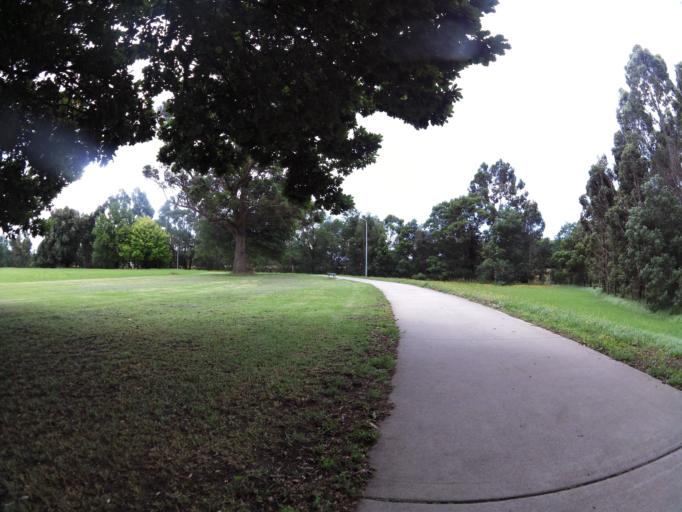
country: AU
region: Victoria
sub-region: Latrobe
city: Traralgon
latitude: -38.1883
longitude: 146.5372
